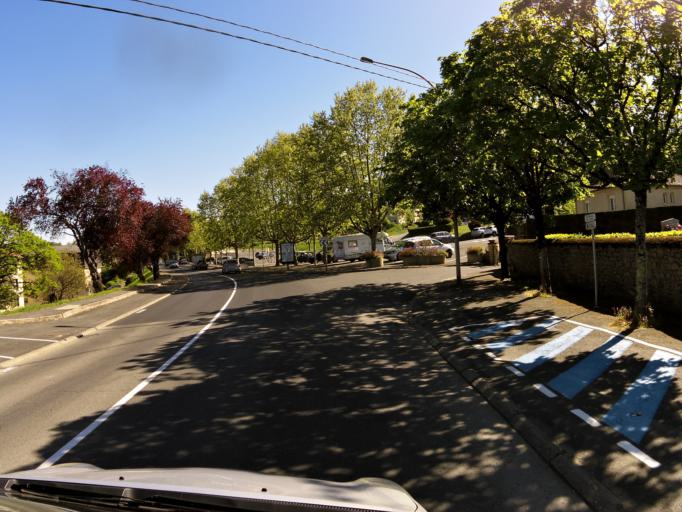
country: FR
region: Aquitaine
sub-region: Departement de la Dordogne
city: Sarlat-la-Caneda
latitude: 44.8937
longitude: 1.2125
